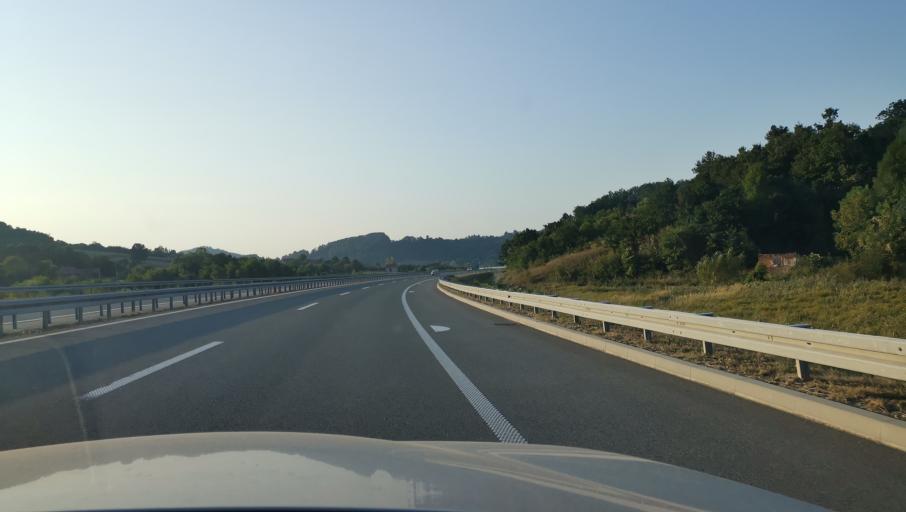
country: RS
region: Central Serbia
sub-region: Kolubarski Okrug
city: Ljig
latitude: 44.1585
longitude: 20.3183
